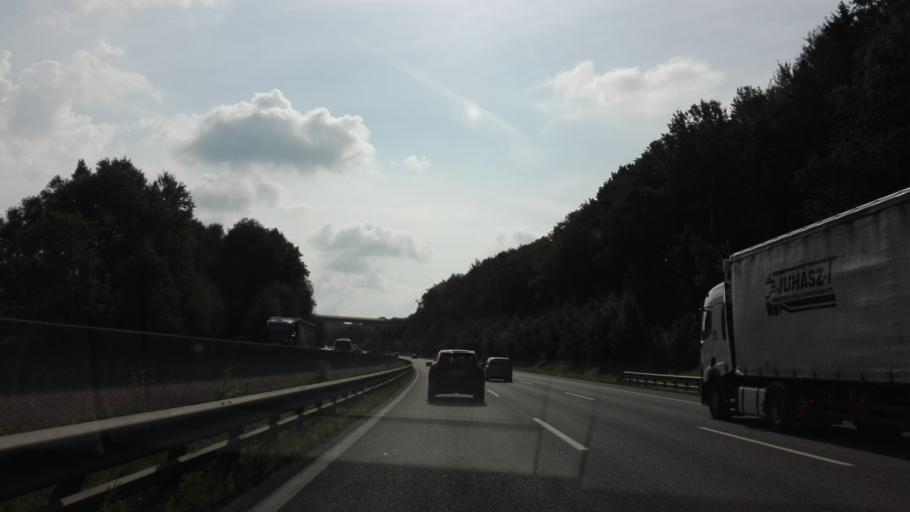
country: AT
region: Lower Austria
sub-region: Politischer Bezirk Amstetten
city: Sankt Georgen am Ybbsfelde
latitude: 48.1386
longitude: 14.9287
